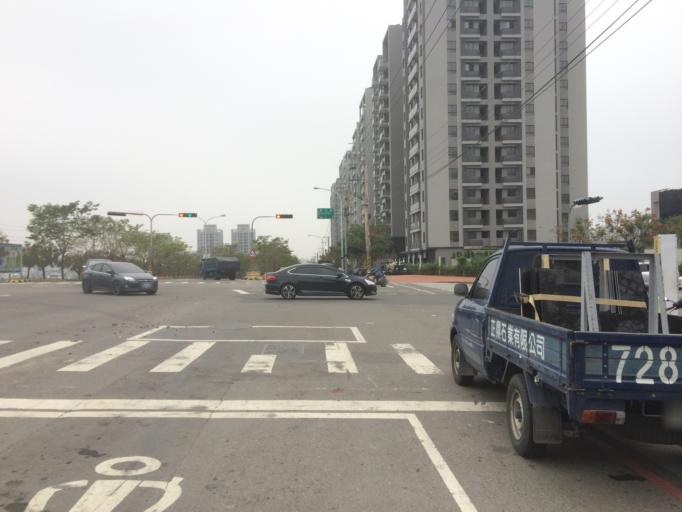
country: TW
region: Taiwan
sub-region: Taichung City
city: Taichung
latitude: 24.1613
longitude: 120.7336
